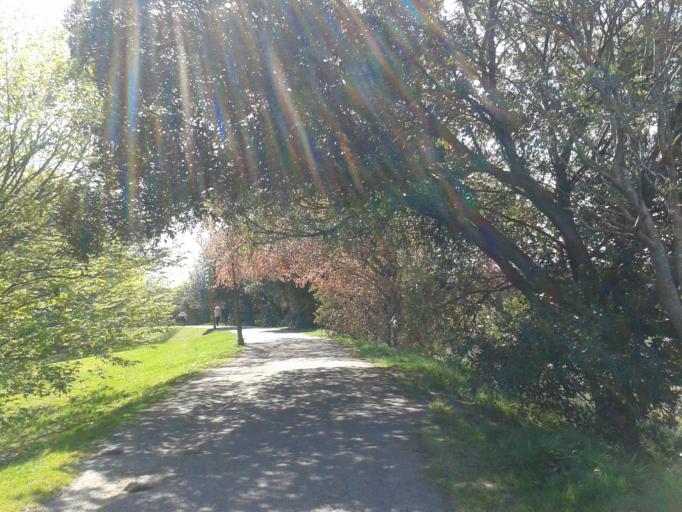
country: GB
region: England
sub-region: Devon
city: Barnstaple
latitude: 51.0697
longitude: -4.0556
